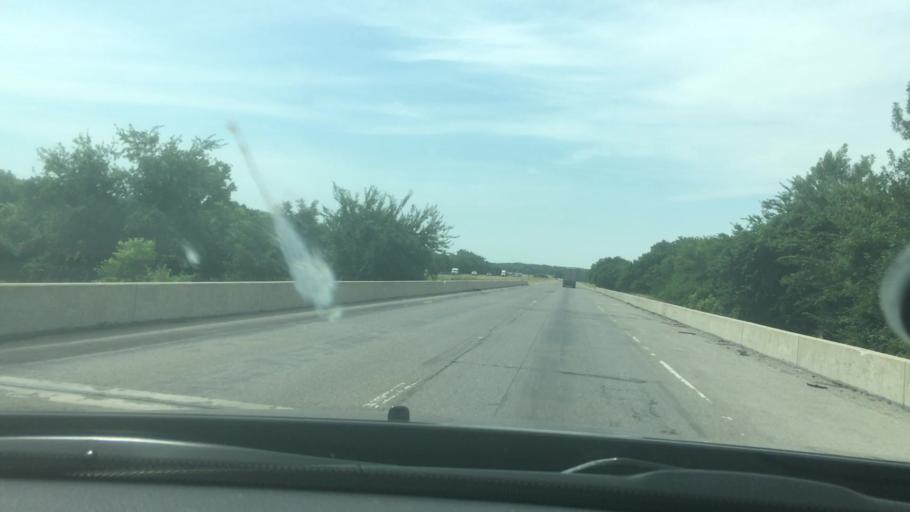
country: US
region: Oklahoma
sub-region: Murray County
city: Davis
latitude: 34.5339
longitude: -97.1878
